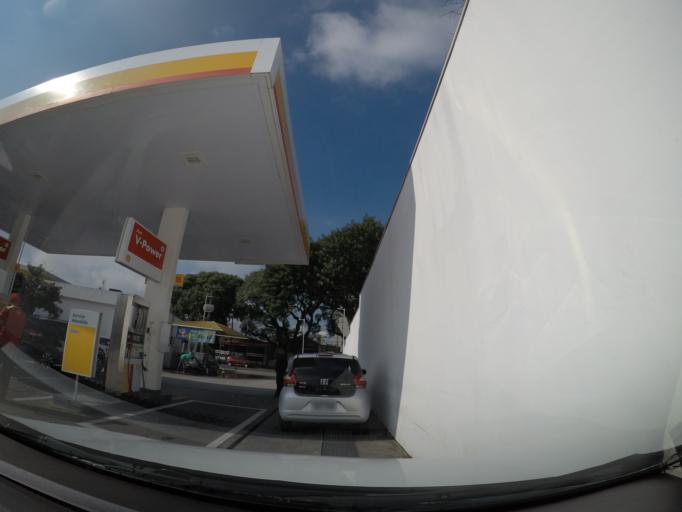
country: BR
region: Parana
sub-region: Curitiba
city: Curitiba
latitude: -25.4384
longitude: -49.2514
